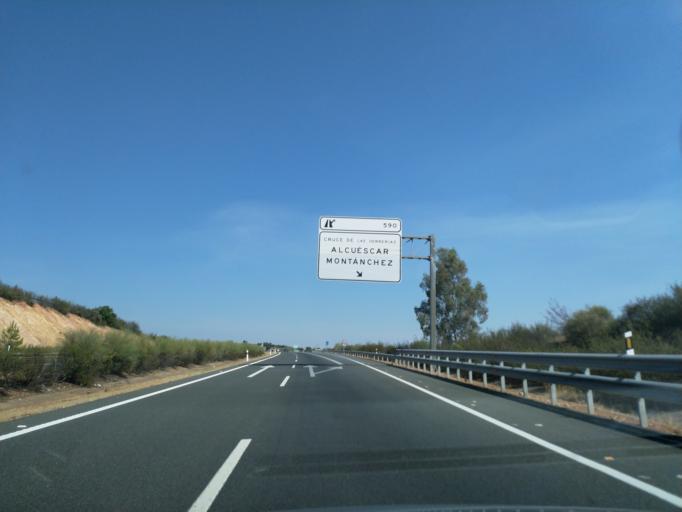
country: ES
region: Extremadura
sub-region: Provincia de Caceres
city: Alcuescar
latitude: 39.1607
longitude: -6.2710
